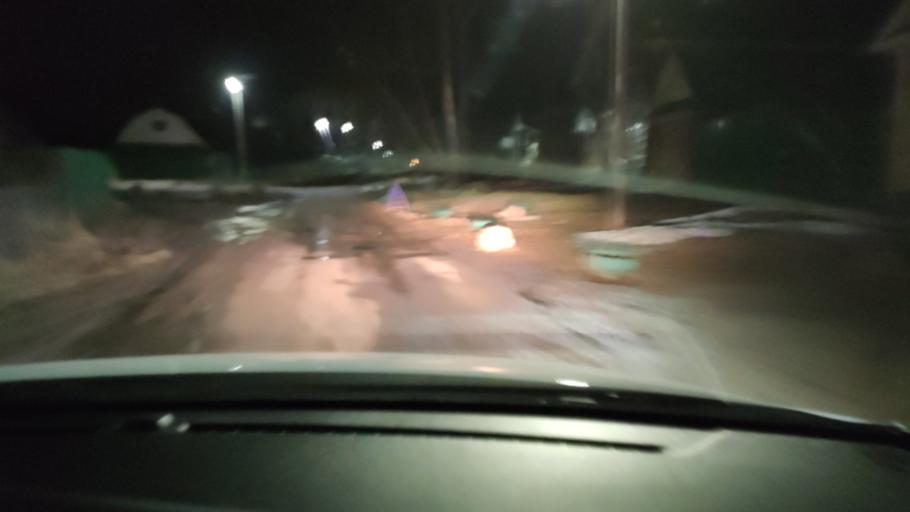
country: RU
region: Tatarstan
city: Vysokaya Gora
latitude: 55.8452
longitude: 49.2169
